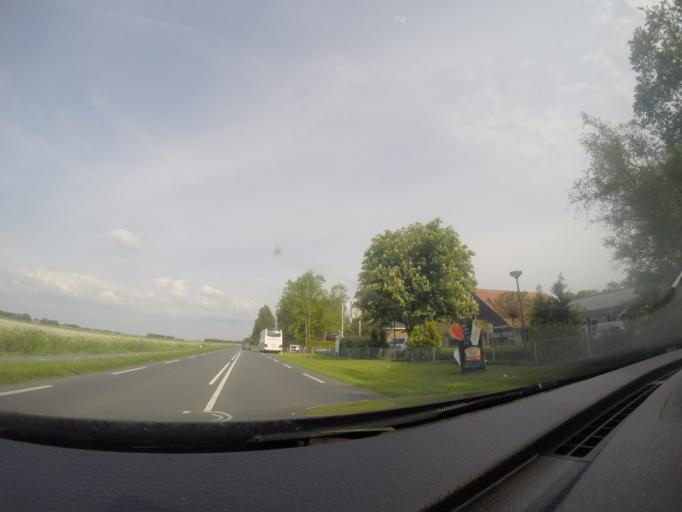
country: NL
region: Flevoland
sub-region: Gemeente Urk
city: Urk
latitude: 52.6496
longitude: 5.6627
